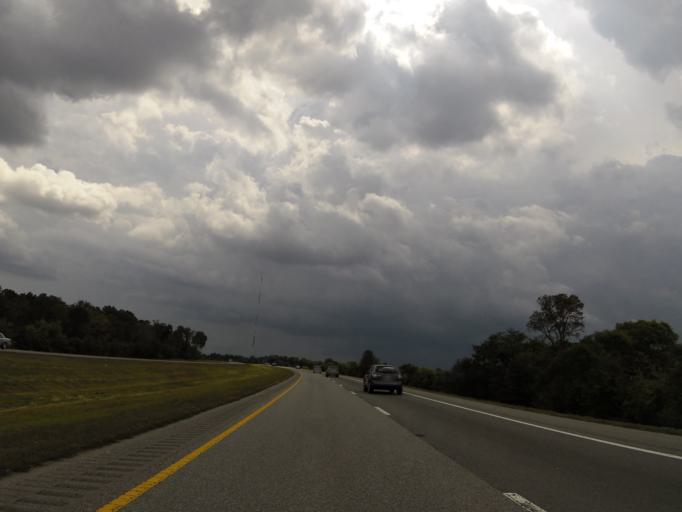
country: US
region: Tennessee
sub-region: Wilson County
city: Rural Hill
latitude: 36.0944
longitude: -86.4242
